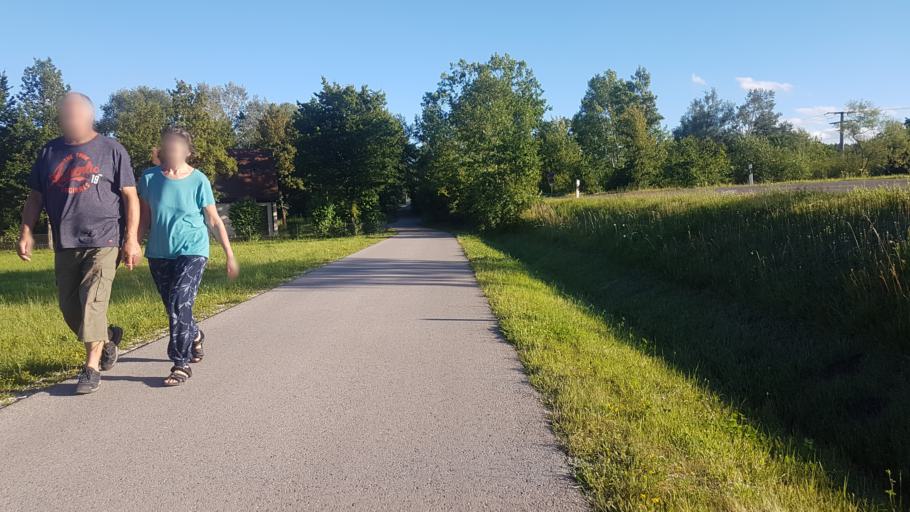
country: DE
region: Bavaria
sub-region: Regierungsbezirk Mittelfranken
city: Absberg
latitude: 49.1304
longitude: 10.8560
